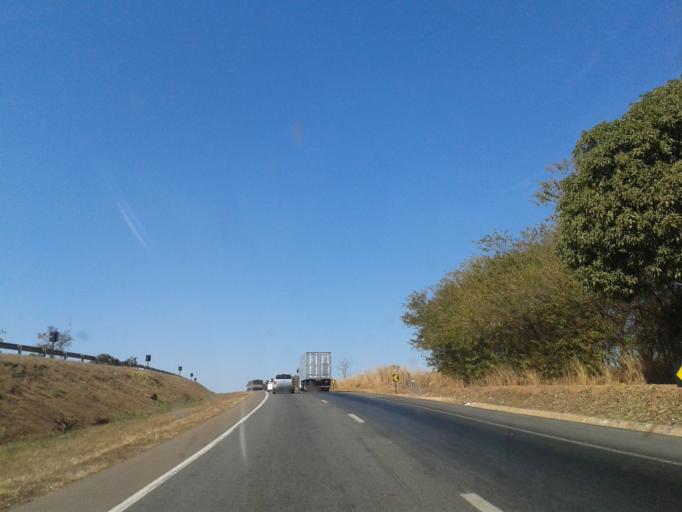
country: BR
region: Goias
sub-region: Aparecida De Goiania
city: Aparecida de Goiania
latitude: -16.8942
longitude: -49.2557
